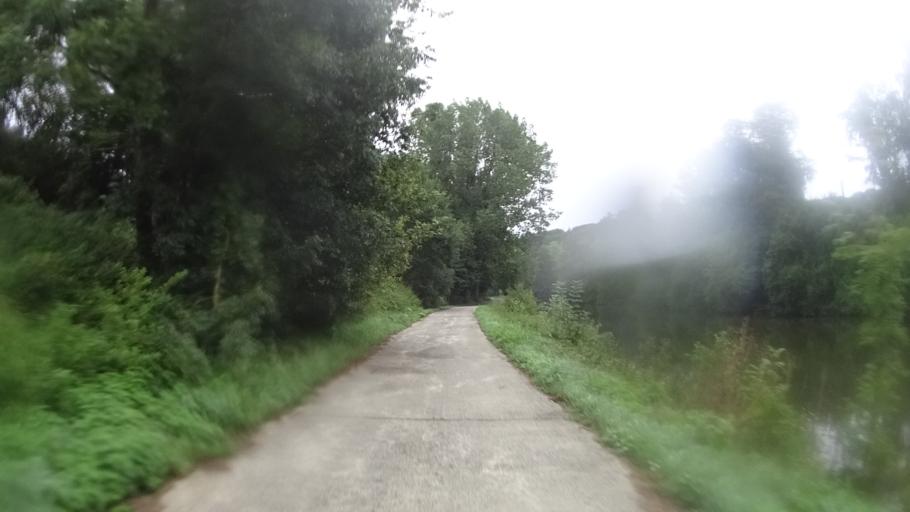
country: BE
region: Wallonia
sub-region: Province du Hainaut
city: Lobbes
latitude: 50.3407
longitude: 4.2454
